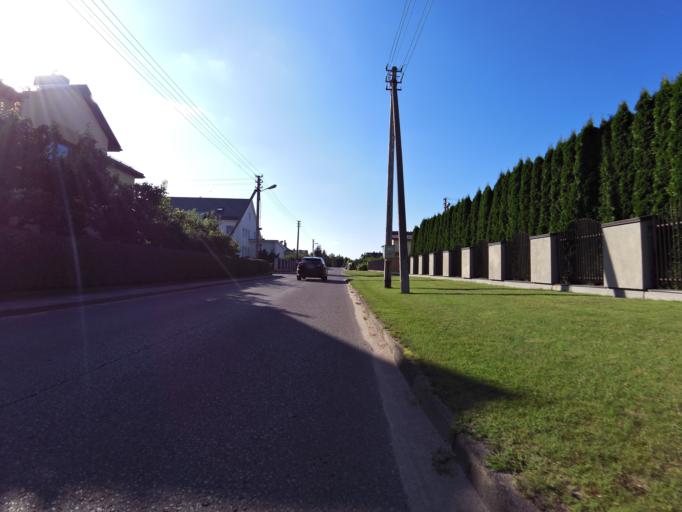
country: LT
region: Vilnius County
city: Pasilaiciai
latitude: 54.7289
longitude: 25.1948
